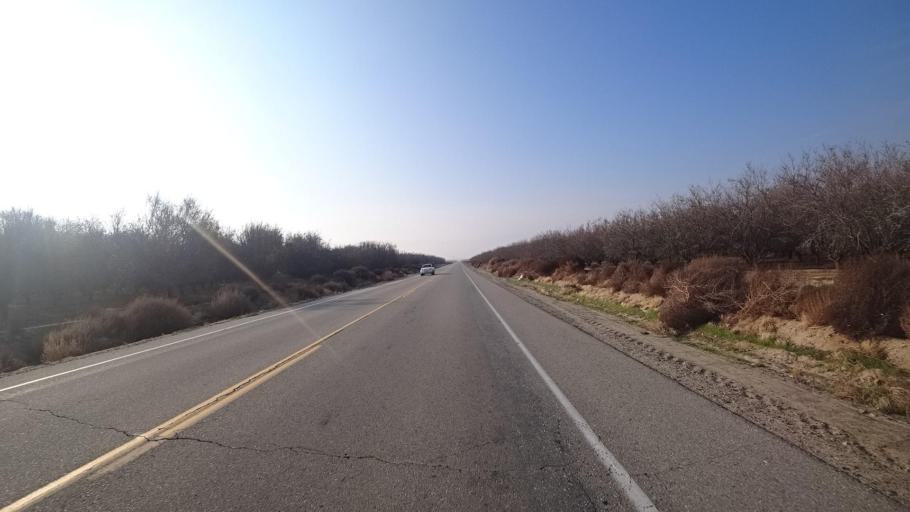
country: US
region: California
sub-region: Kern County
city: Arvin
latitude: 35.0424
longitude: -118.9190
